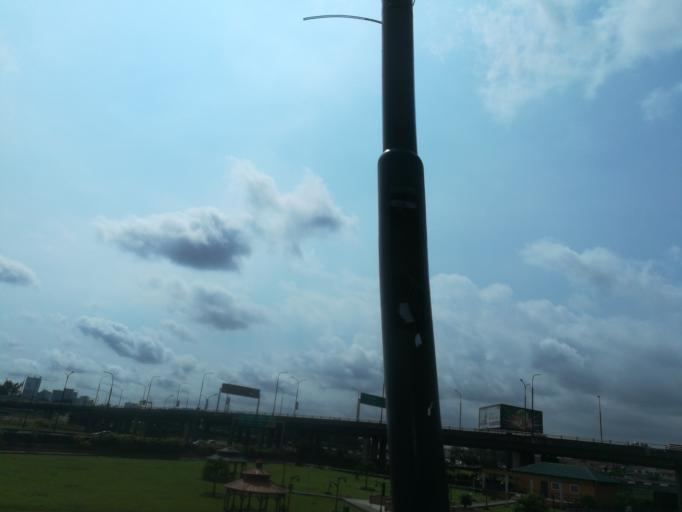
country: NG
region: Lagos
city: Lagos
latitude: 6.4559
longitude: 3.4092
